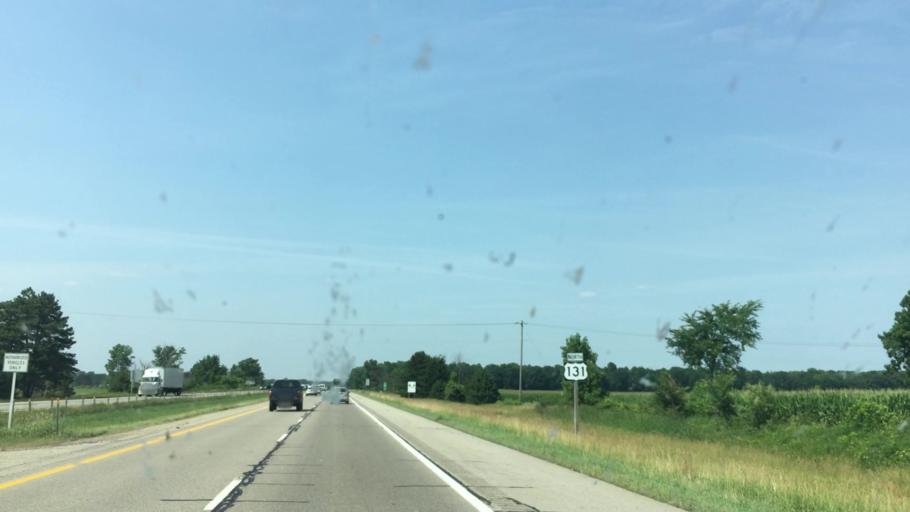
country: US
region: Michigan
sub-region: Allegan County
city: Wayland
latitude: 42.6368
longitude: -85.6621
